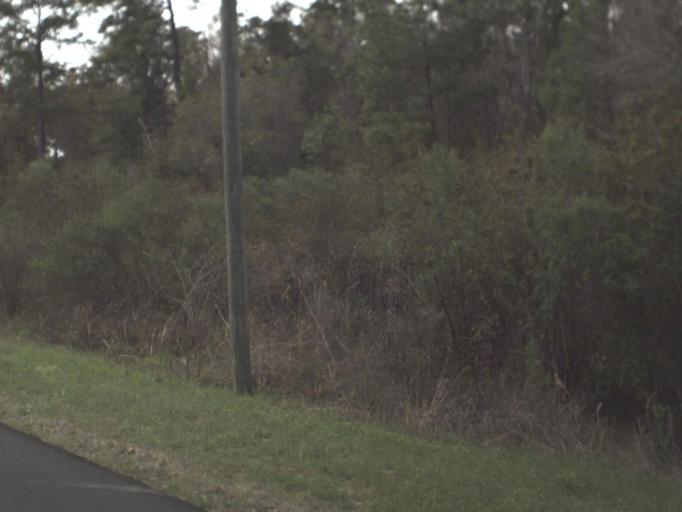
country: US
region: Florida
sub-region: Gadsden County
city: Midway
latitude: 30.4007
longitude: -84.5944
